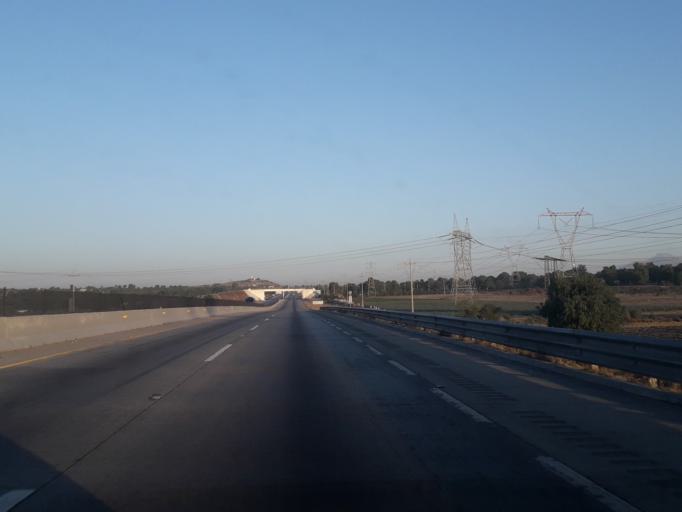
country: MX
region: Puebla
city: Acatzingo de Hidalgo
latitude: 18.9658
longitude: -97.7779
